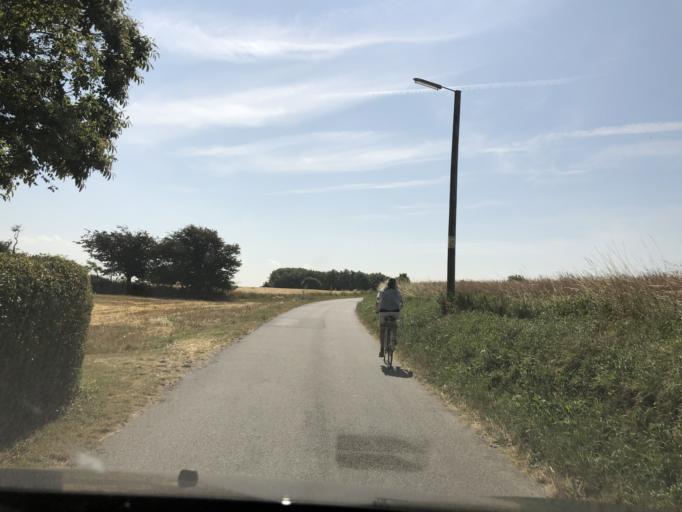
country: DK
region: South Denmark
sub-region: Faaborg-Midtfyn Kommune
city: Faaborg
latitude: 54.9513
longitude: 10.2293
